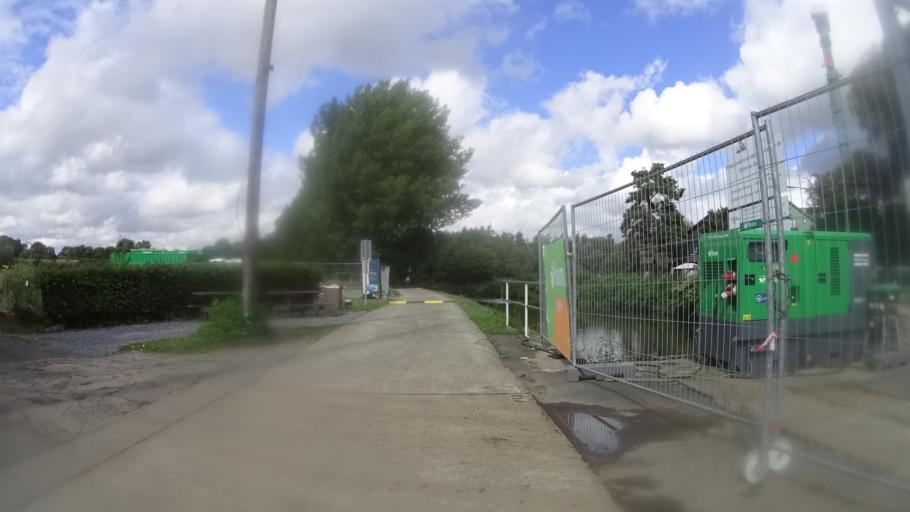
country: BE
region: Wallonia
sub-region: Province du Hainaut
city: Merbes-le-Chateau
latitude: 50.3099
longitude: 4.1498
